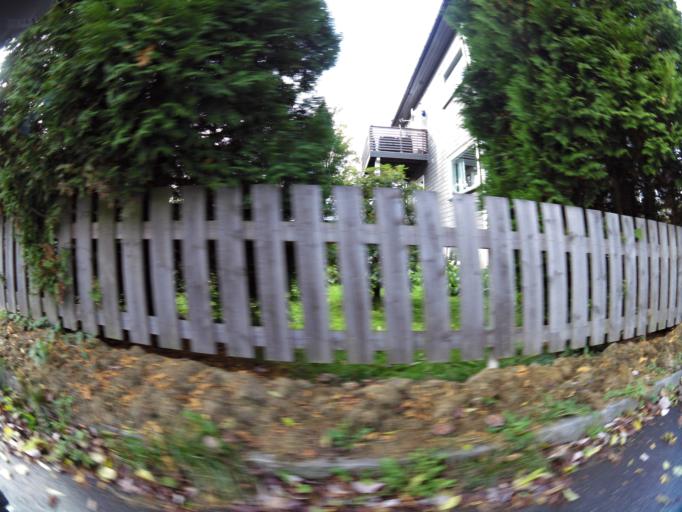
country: NO
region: Ostfold
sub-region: Fredrikstad
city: Fredrikstad
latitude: 59.2251
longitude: 10.9293
